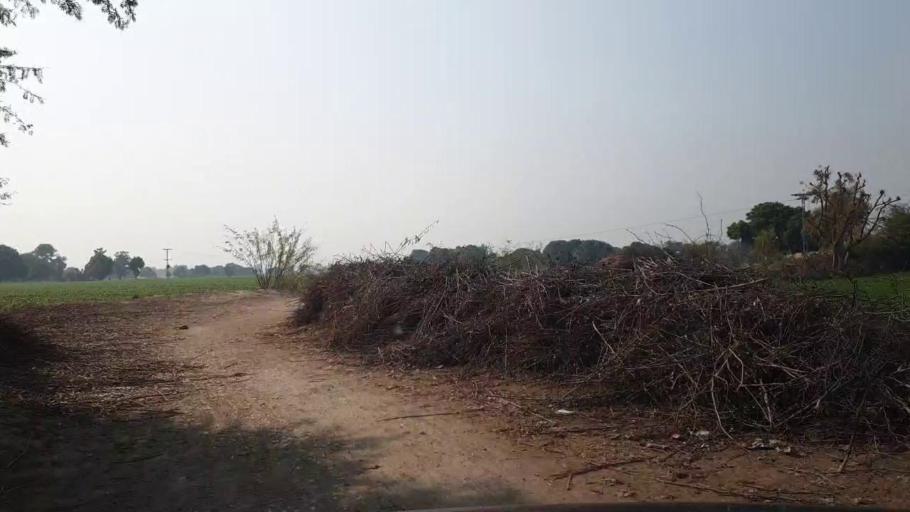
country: PK
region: Sindh
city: Hala
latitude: 25.8450
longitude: 68.4271
